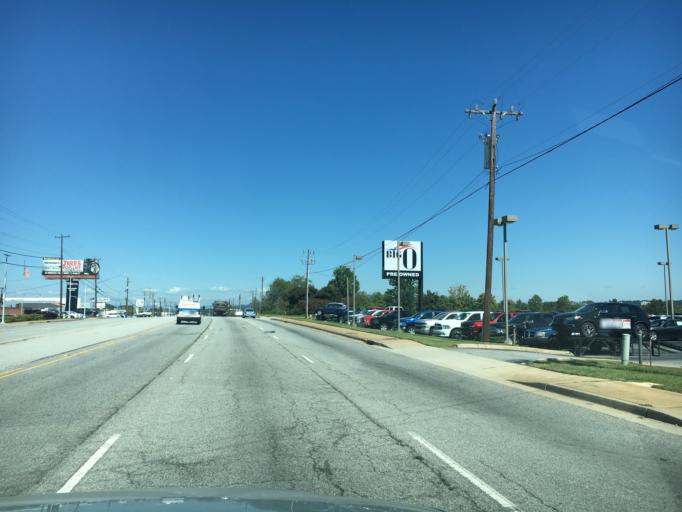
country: US
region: South Carolina
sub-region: Greenville County
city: Mauldin
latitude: 34.8226
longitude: -82.3427
